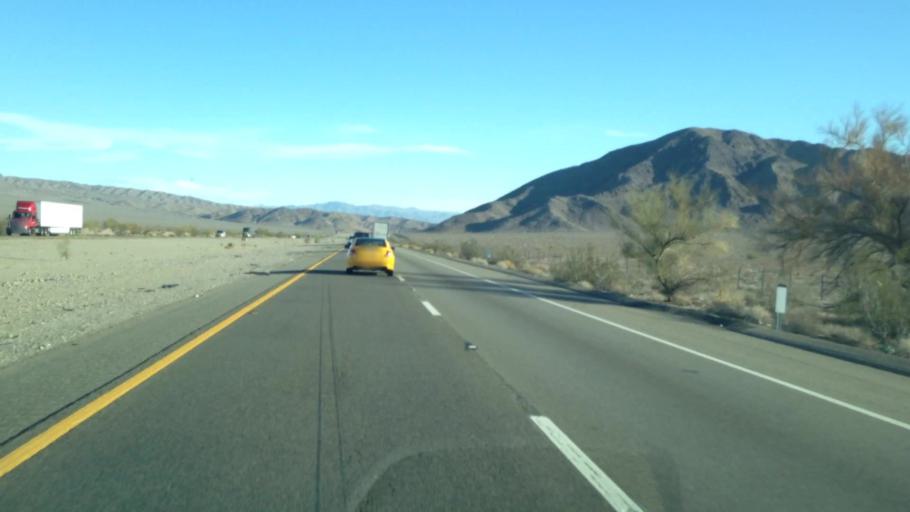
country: US
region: California
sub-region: San Bernardino County
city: Fort Irwin
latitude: 35.1718
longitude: -116.1764
